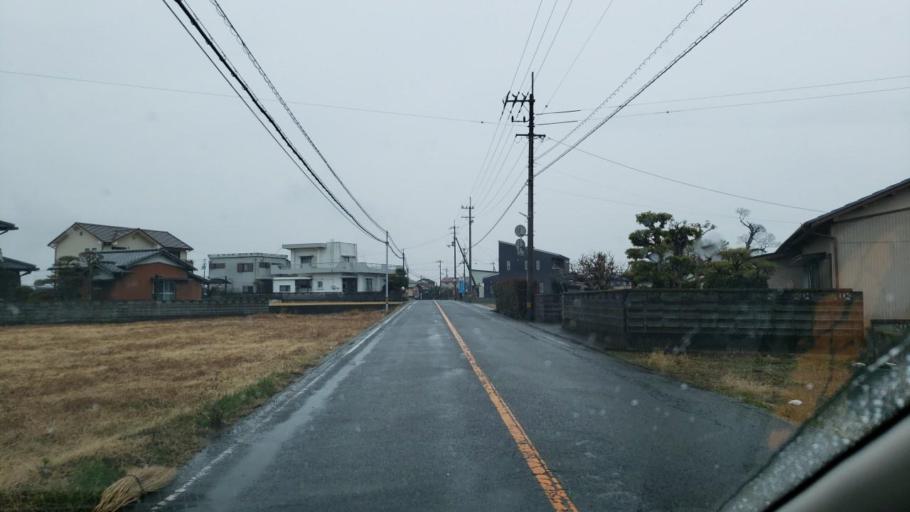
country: JP
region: Tokushima
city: Kamojimacho-jogejima
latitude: 34.0963
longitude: 134.3544
